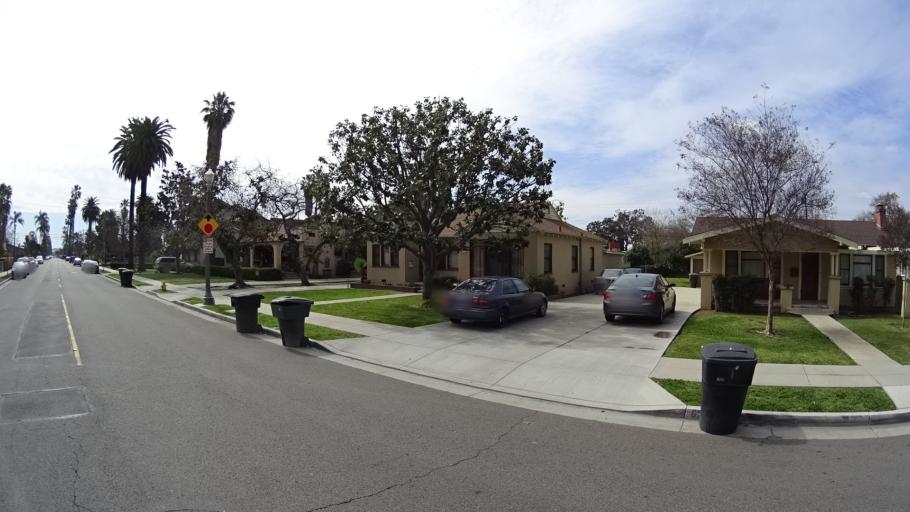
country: US
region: California
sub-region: Orange County
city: Anaheim
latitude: 33.8274
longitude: -117.9133
